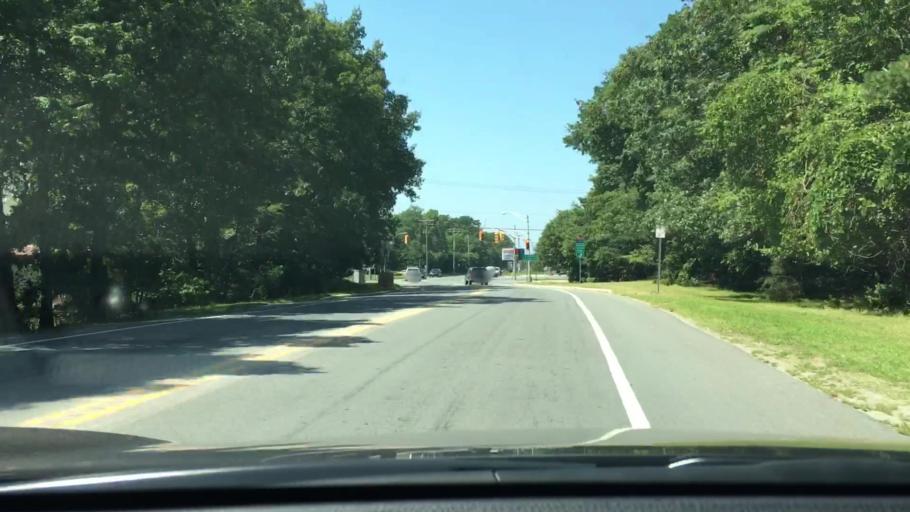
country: US
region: New Jersey
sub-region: Cumberland County
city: Laurel Lake
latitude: 39.2905
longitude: -74.9673
